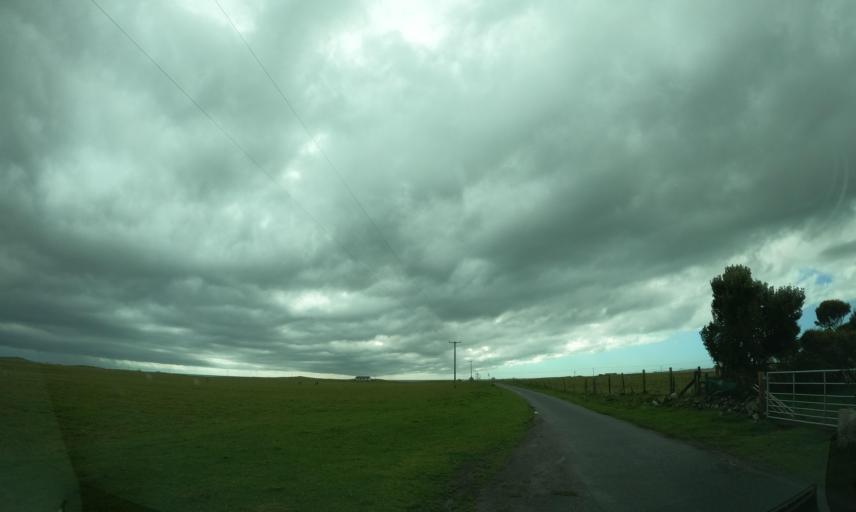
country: GB
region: Scotland
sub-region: Eilean Siar
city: Barra
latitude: 56.5319
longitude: -6.7977
